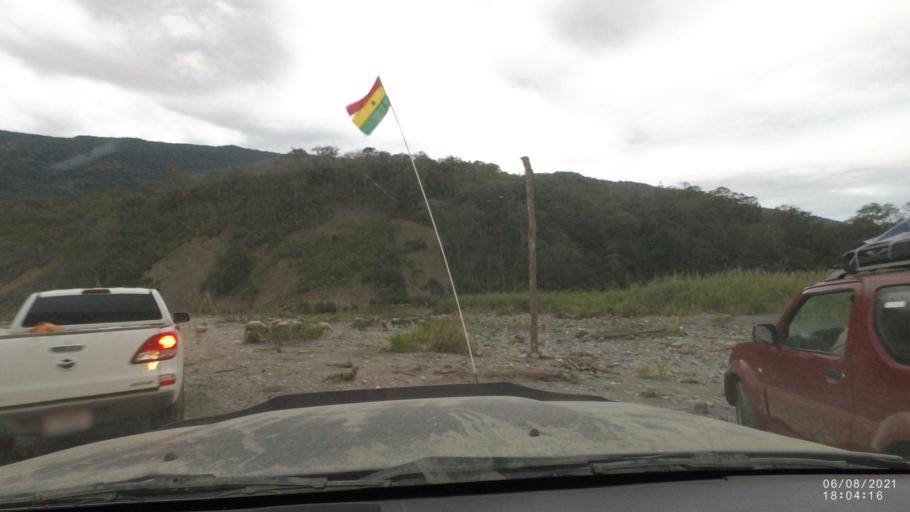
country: BO
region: La Paz
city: Quime
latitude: -16.4721
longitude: -66.7862
